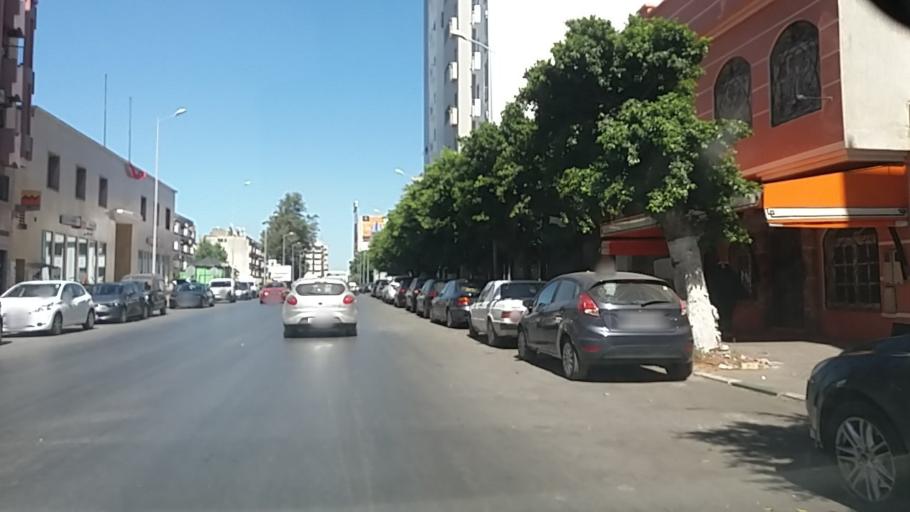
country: MA
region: Gharb-Chrarda-Beni Hssen
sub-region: Kenitra Province
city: Kenitra
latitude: 34.2619
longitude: -6.5844
